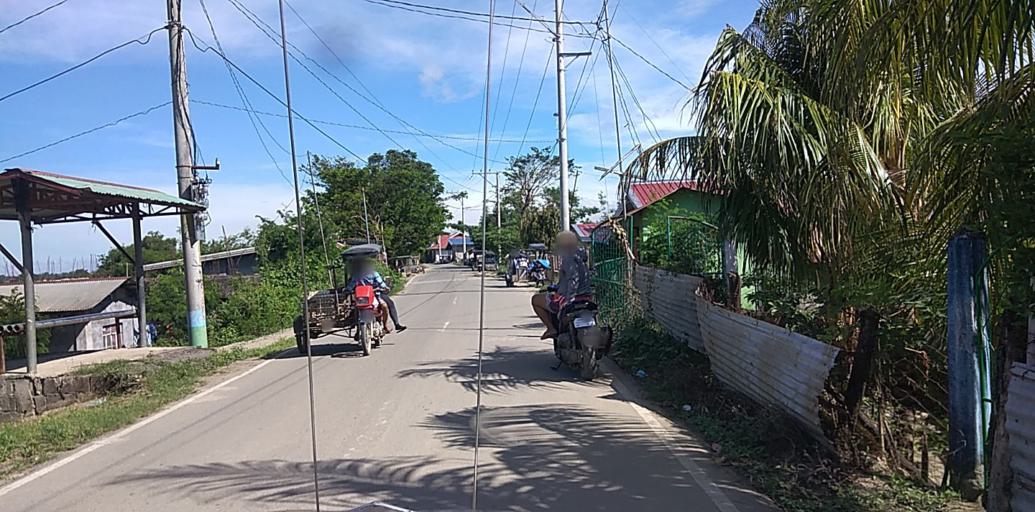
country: PH
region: Central Luzon
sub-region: Province of Pampanga
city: San Nicolas
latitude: 15.0668
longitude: 120.8047
